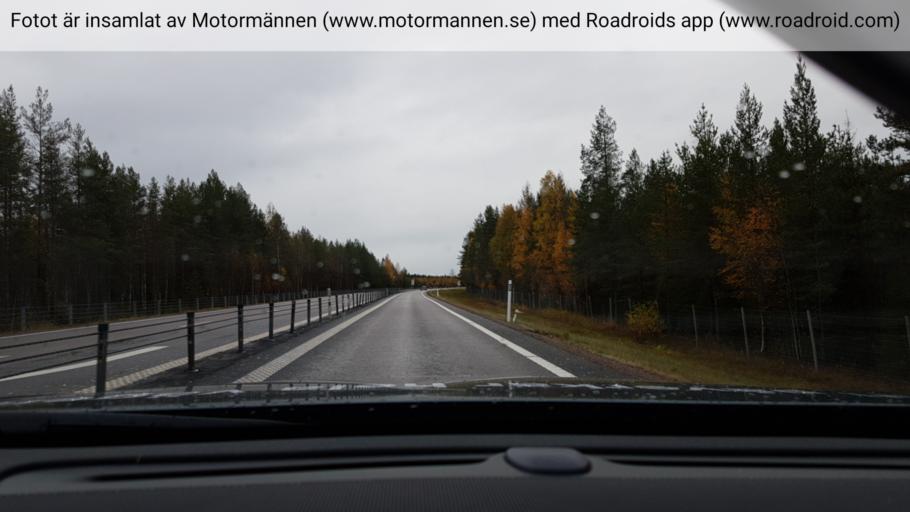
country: SE
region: Norrbotten
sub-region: Pitea Kommun
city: Rosvik
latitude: 65.4972
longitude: 21.7661
